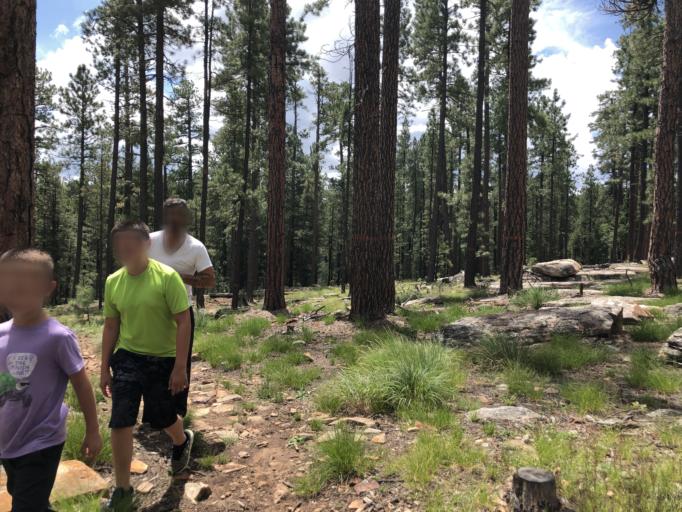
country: US
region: Arizona
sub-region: Gila County
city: Star Valley
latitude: 34.3340
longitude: -110.9479
